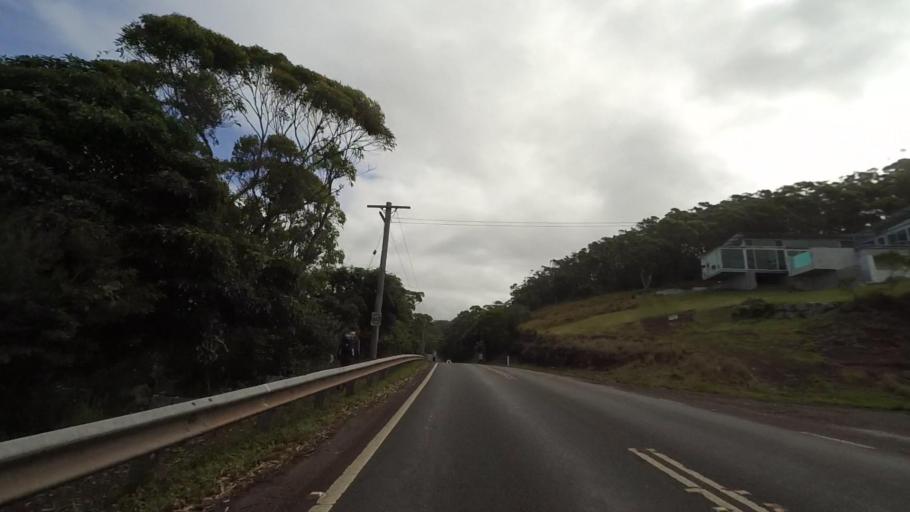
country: AU
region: New South Wales
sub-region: Wollongong
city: Helensburgh
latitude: -34.2118
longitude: 151.0096
